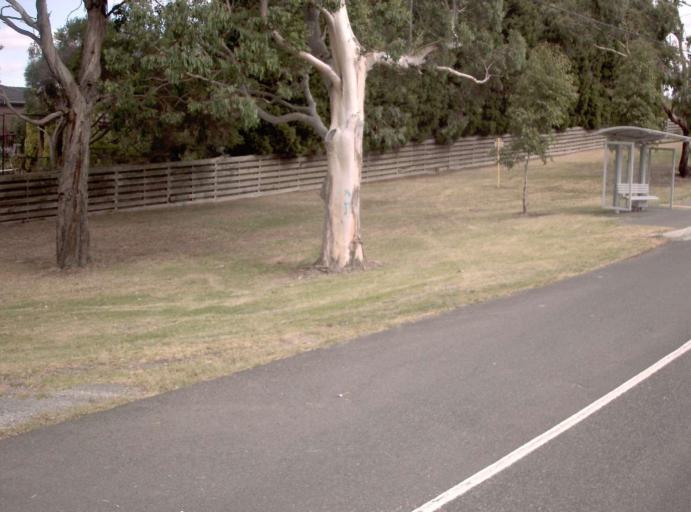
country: AU
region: Victoria
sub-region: Knox
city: Rowville
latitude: -37.9529
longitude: 145.2269
